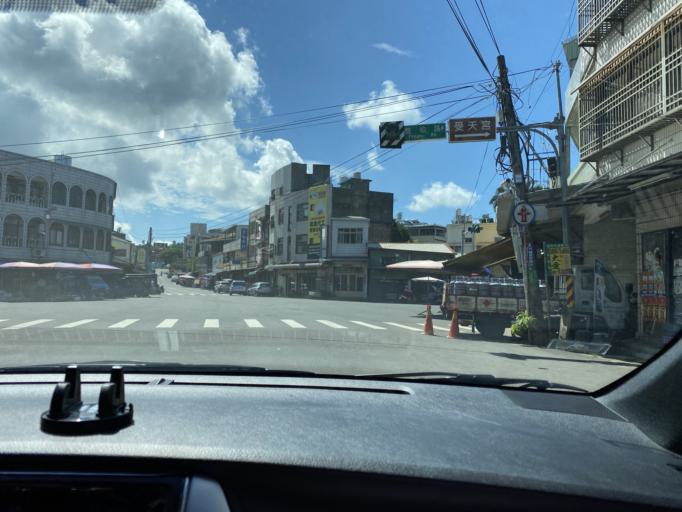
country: TW
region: Taiwan
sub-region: Nantou
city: Nantou
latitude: 23.8350
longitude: 120.6346
